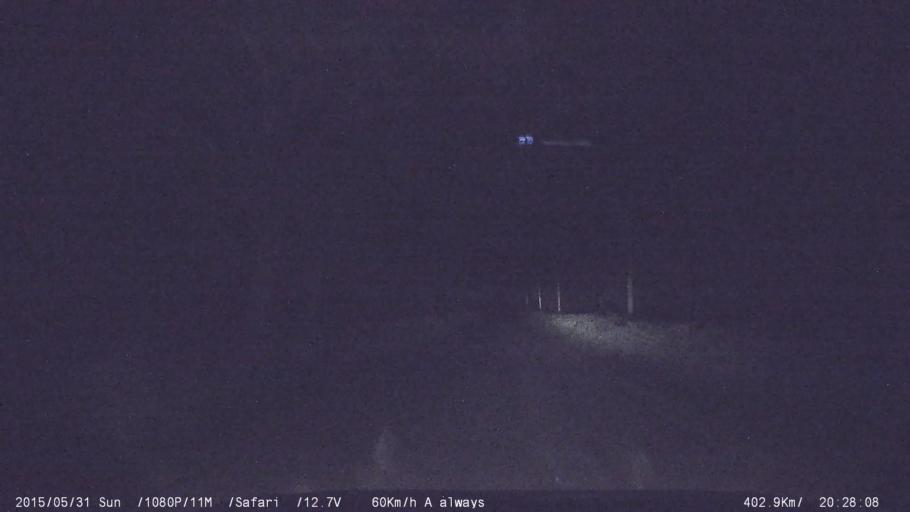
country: IN
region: Karnataka
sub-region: Mandya
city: Malavalli
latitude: 12.4458
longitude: 77.2316
